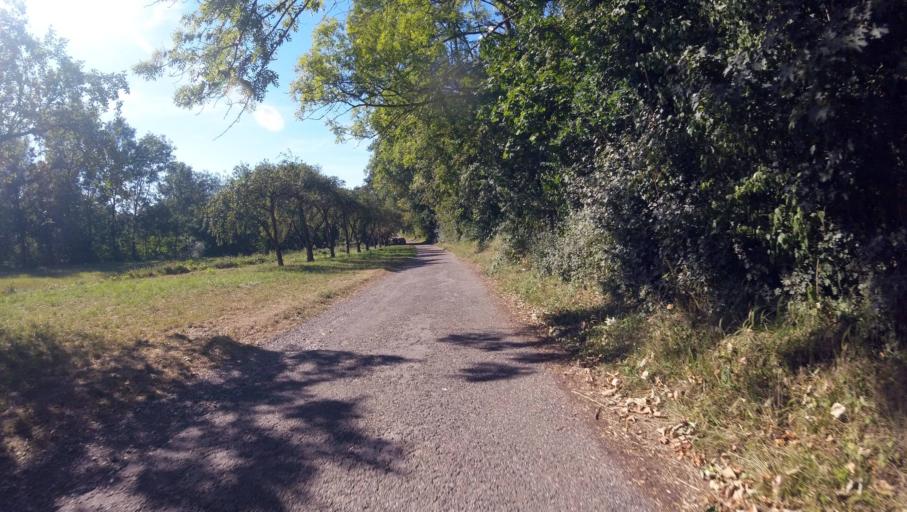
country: DE
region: Baden-Wuerttemberg
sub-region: Regierungsbezirk Stuttgart
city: Kirchberg an der Murr
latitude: 48.9396
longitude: 9.3364
